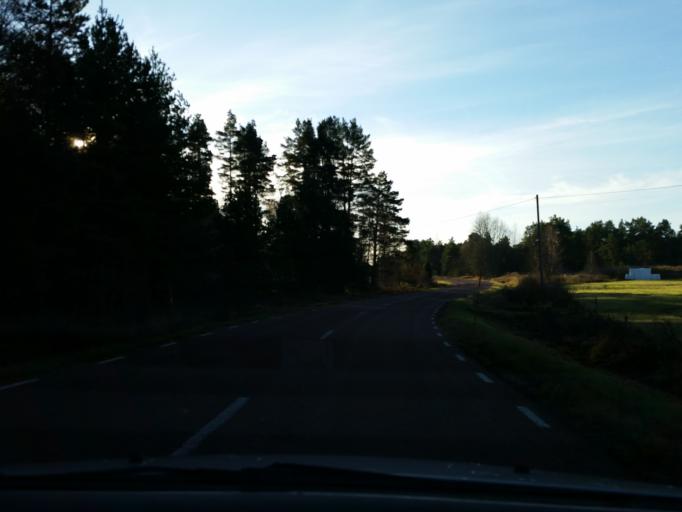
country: AX
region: Alands landsbygd
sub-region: Saltvik
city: Saltvik
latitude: 60.2594
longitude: 20.0630
